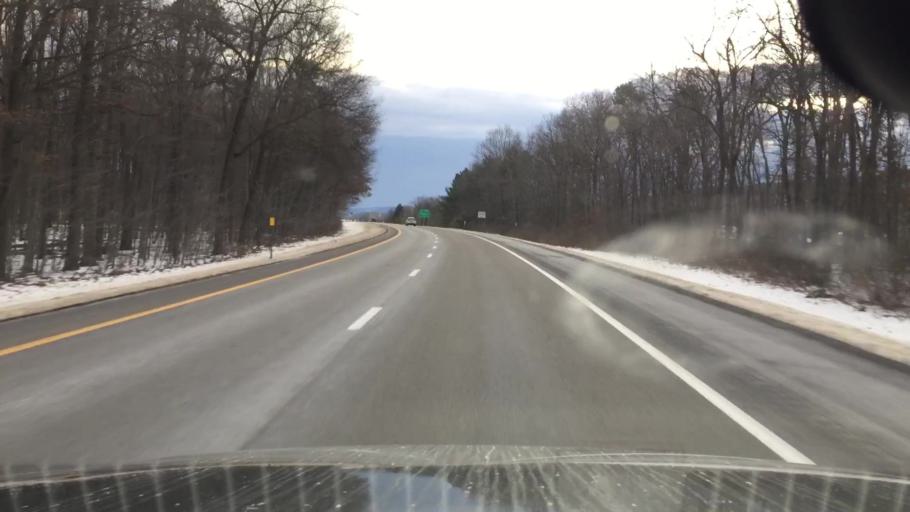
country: US
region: Pennsylvania
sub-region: Bradford County
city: South Waverly
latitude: 42.0010
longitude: -76.6171
